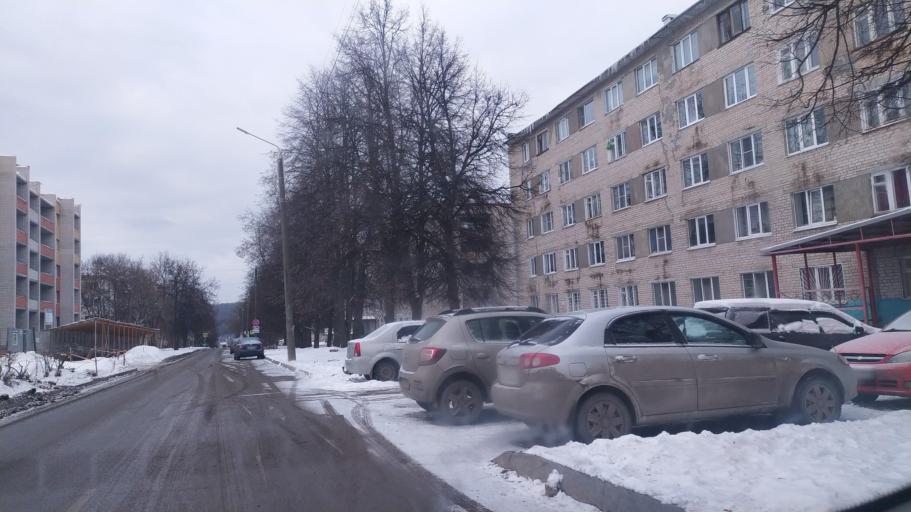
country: RU
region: Chuvashia
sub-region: Cheboksarskiy Rayon
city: Cheboksary
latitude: 56.1239
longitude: 47.2003
